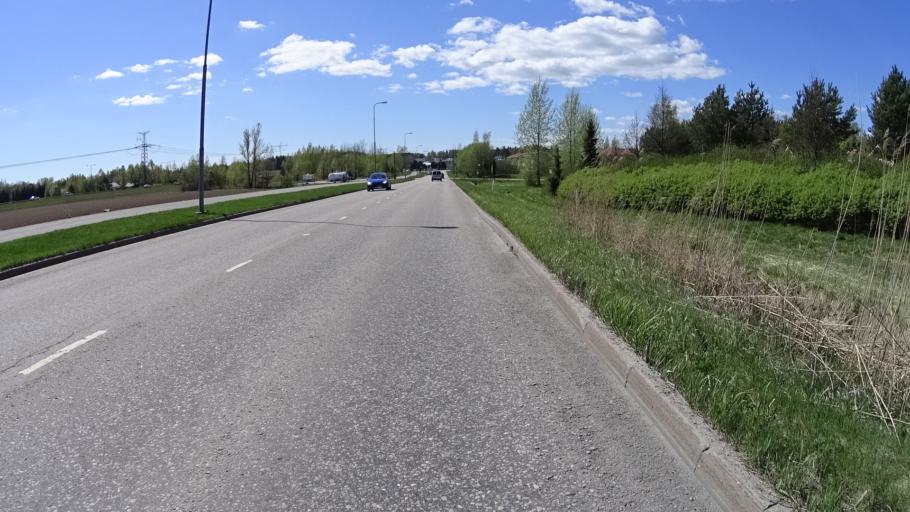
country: FI
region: Uusimaa
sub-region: Helsinki
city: Kilo
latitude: 60.2685
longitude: 24.7522
